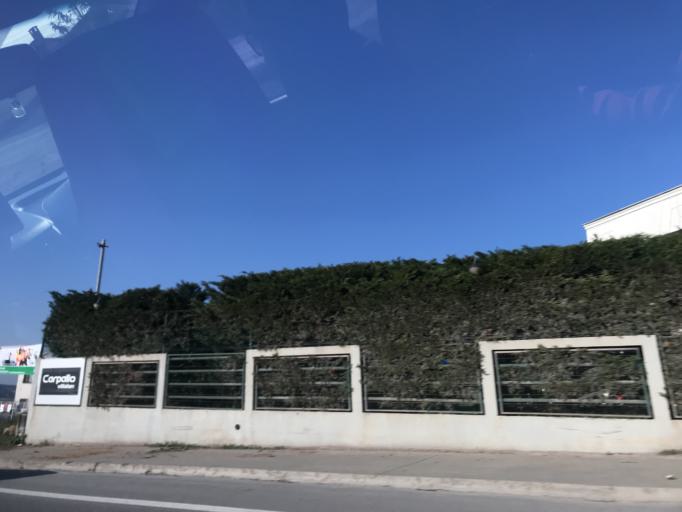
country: TR
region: Kocaeli
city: Balcik
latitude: 40.9426
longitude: 29.3746
